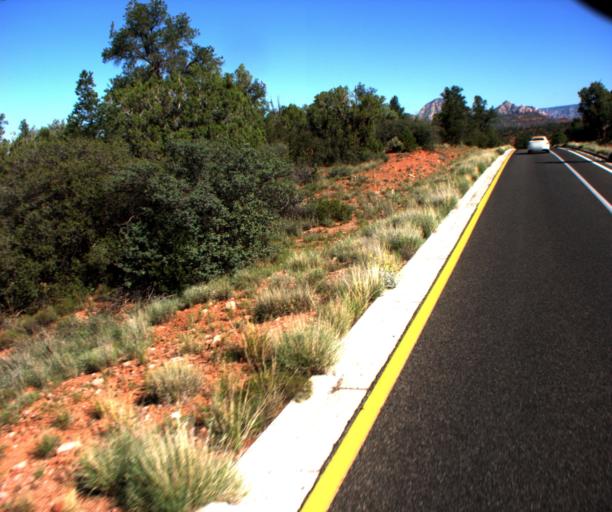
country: US
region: Arizona
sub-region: Yavapai County
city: Village of Oak Creek (Big Park)
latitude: 34.8139
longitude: -111.7660
